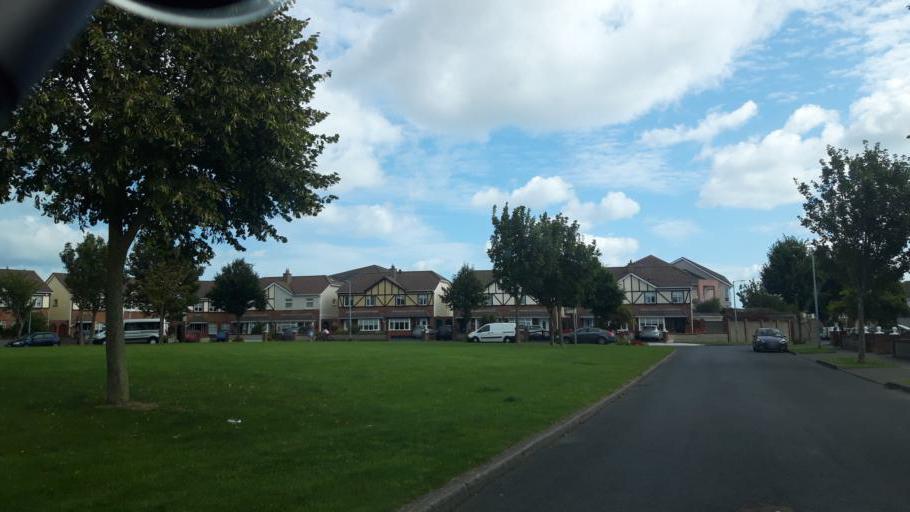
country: IE
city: Darndale
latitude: 53.3981
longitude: -6.1823
